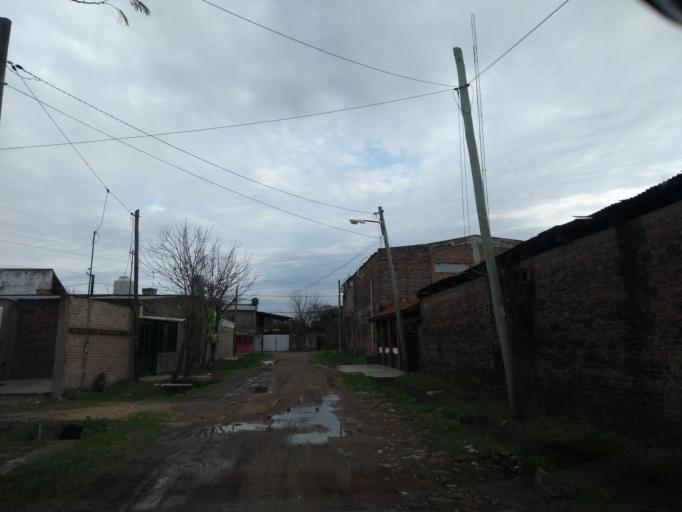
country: AR
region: Chaco
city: Resistencia
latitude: -27.4759
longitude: -58.9738
